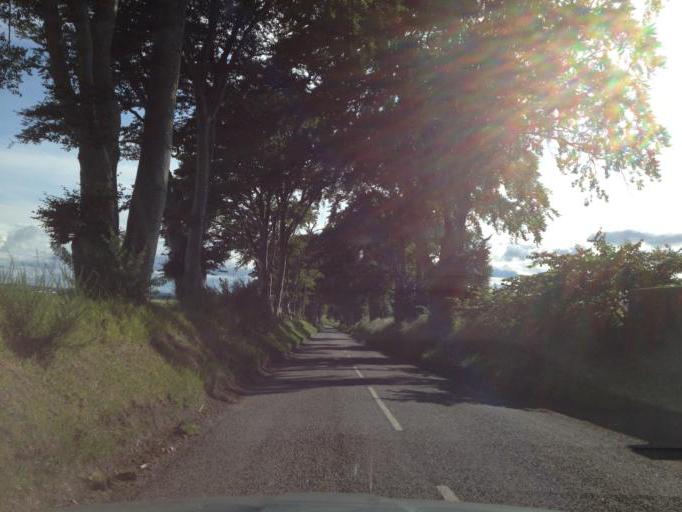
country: GB
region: Scotland
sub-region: Aberdeenshire
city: Laurencekirk
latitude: 56.8483
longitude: -2.5838
